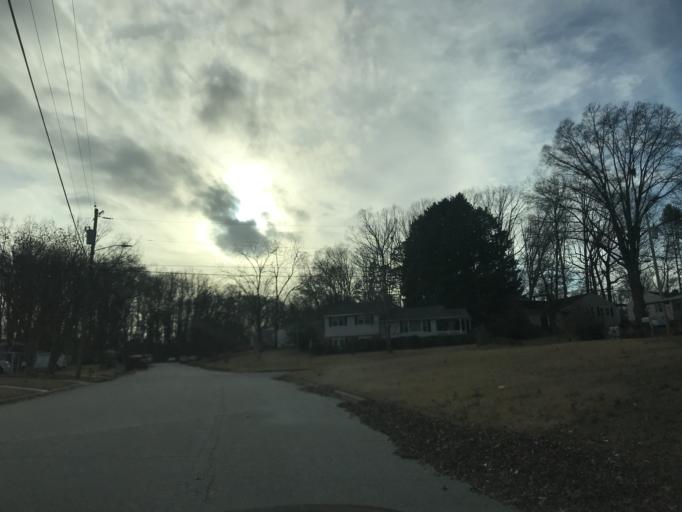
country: US
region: North Carolina
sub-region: Wake County
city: Raleigh
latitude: 35.8003
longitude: -78.6113
